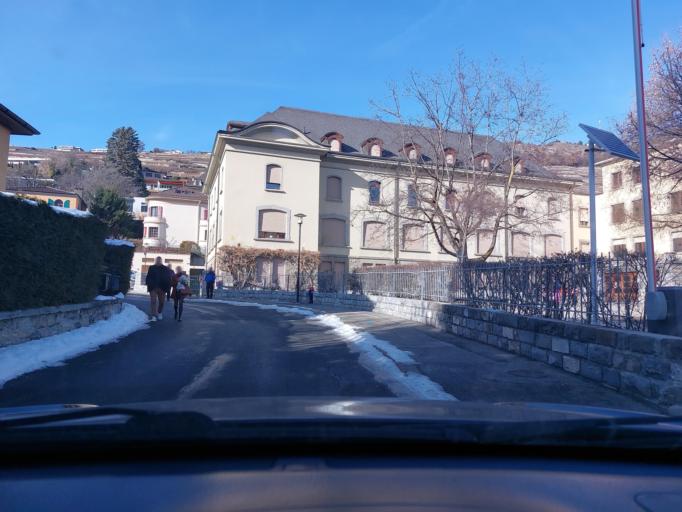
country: CH
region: Valais
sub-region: Sion District
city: Sitten
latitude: 46.2355
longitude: 7.3558
